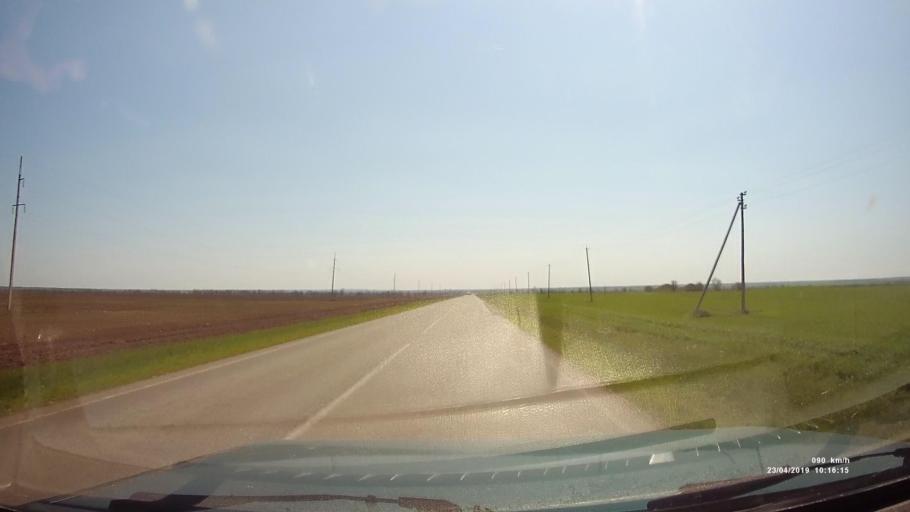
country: RU
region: Rostov
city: Sovetskoye
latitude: 46.6597
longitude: 42.3924
